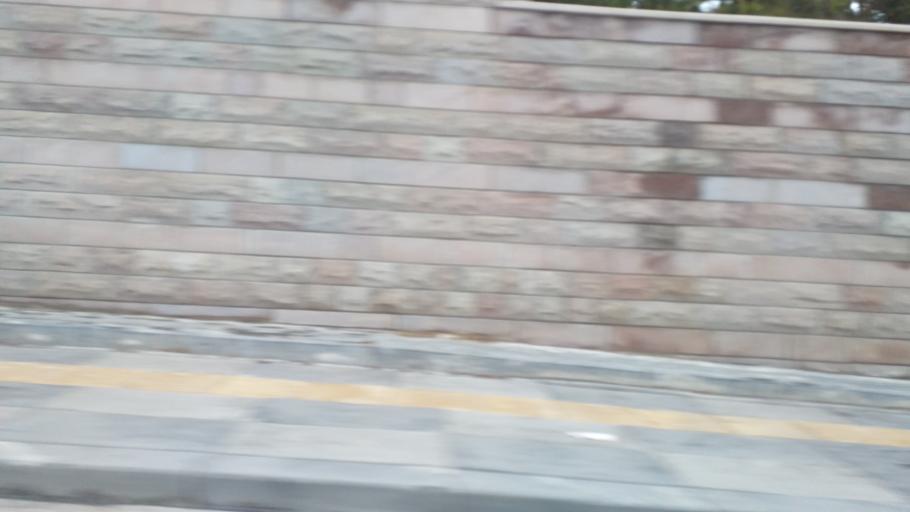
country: TR
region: Ankara
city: Ankara
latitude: 39.9320
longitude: 32.8195
